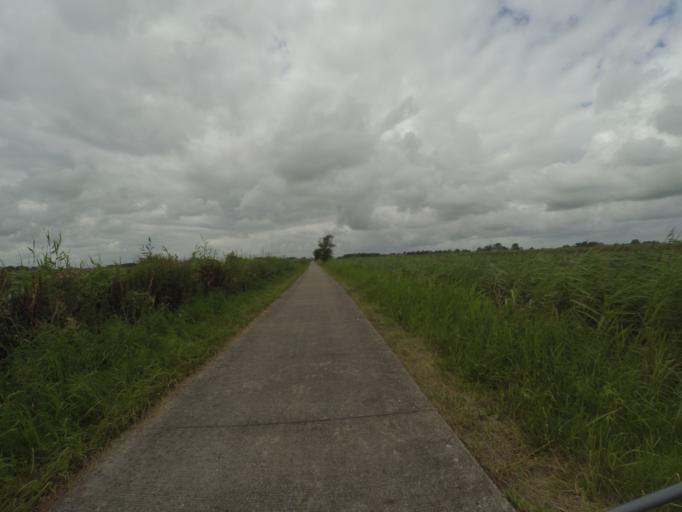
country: NL
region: Friesland
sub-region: Gemeente Dongeradeel
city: Anjum
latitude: 53.3211
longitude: 6.1200
